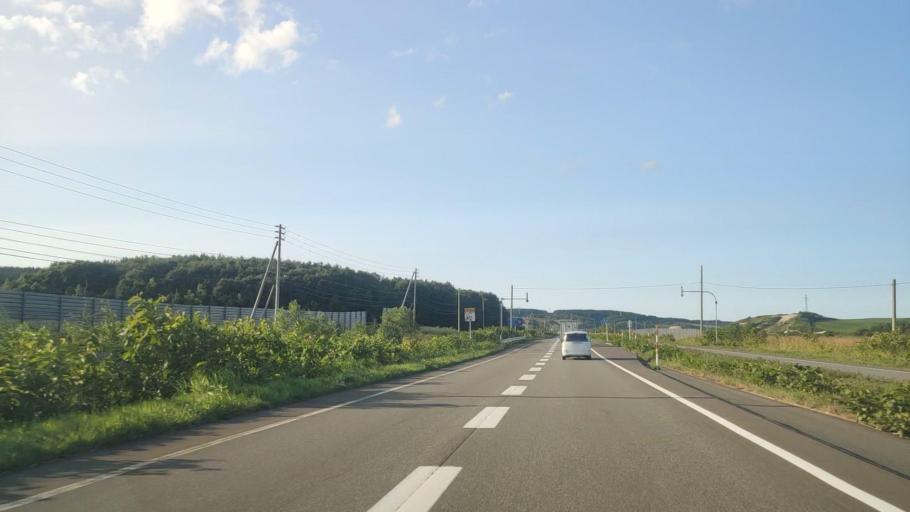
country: JP
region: Hokkaido
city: Wakkanai
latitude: 45.3230
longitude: 141.7195
